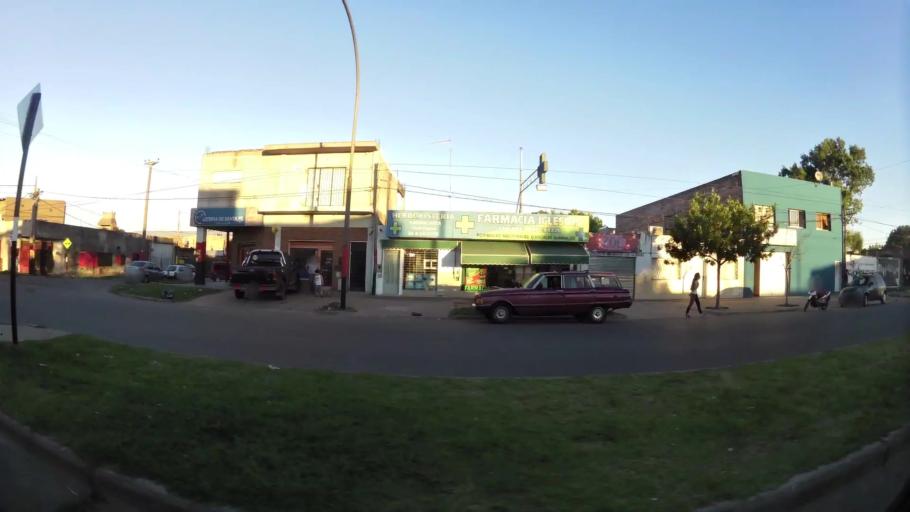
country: AR
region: Santa Fe
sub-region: Departamento de Rosario
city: Rosario
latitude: -32.9674
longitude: -60.6864
